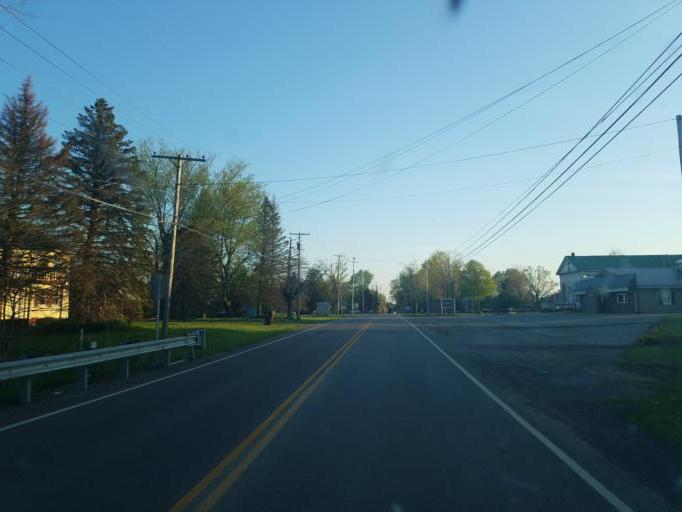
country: US
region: Ohio
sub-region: Ashtabula County
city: Andover
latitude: 41.4567
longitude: -80.5786
